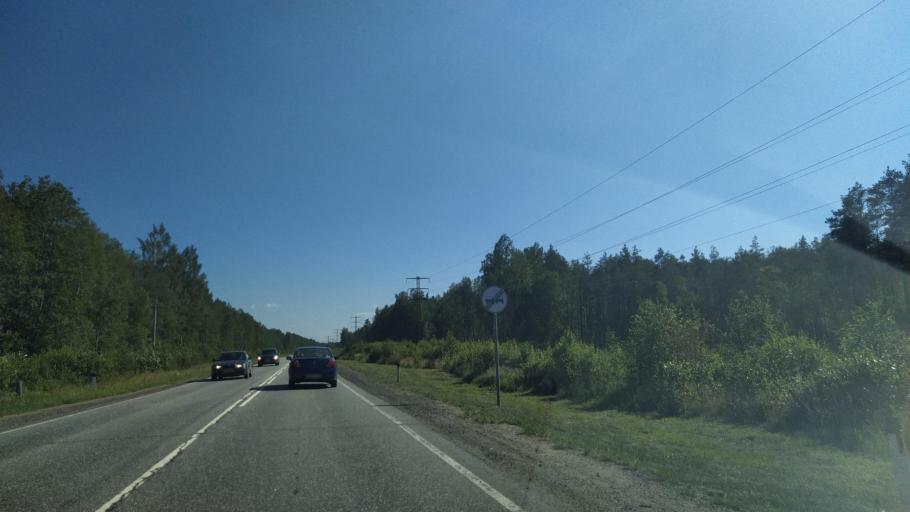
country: RU
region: Leningrad
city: Imeni Morozova
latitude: 60.0289
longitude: 31.0373
